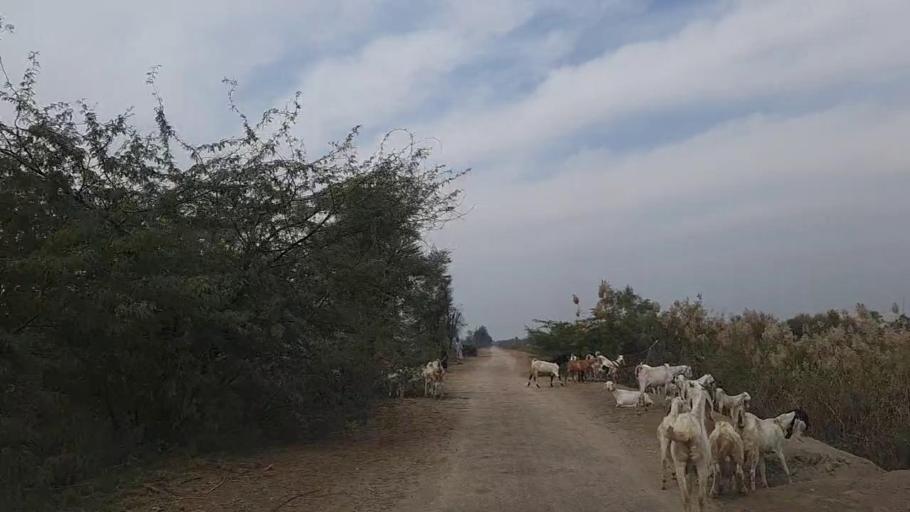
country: PK
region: Sindh
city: Daur
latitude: 26.4355
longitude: 68.4635
